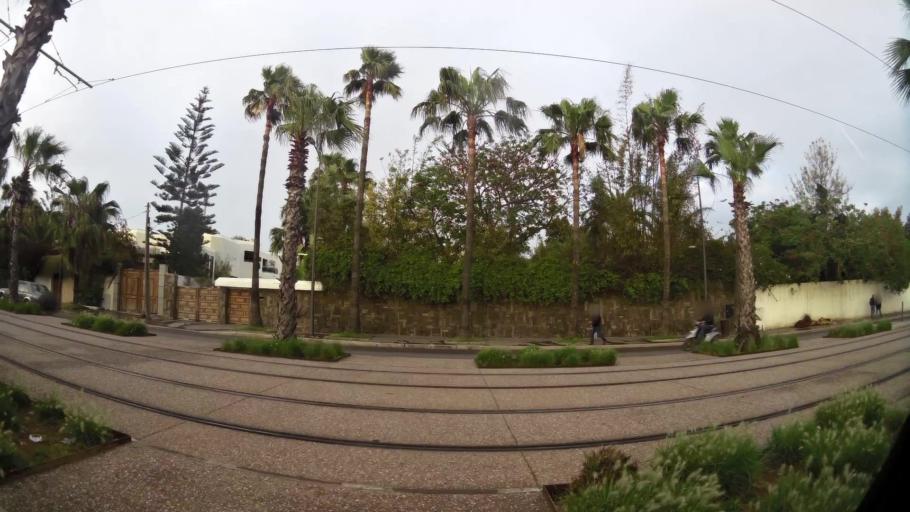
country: MA
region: Grand Casablanca
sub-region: Casablanca
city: Casablanca
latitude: 33.5785
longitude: -7.6741
